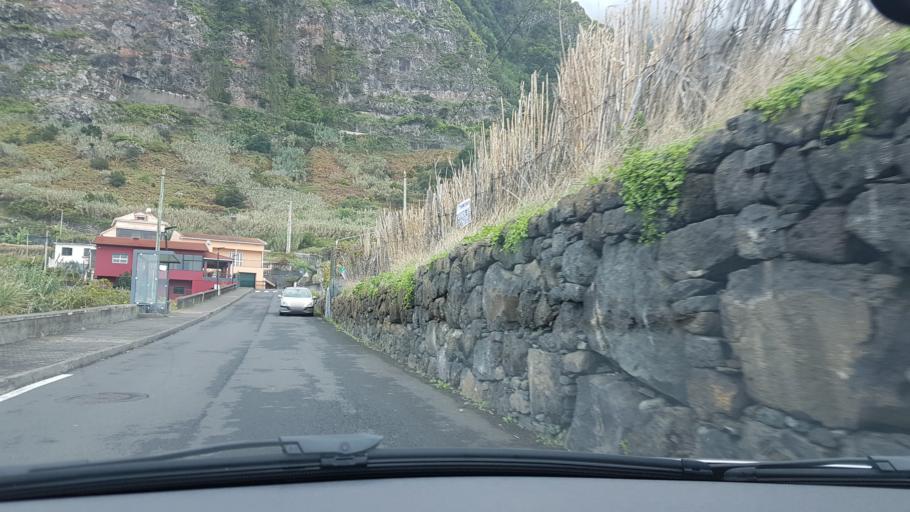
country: PT
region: Madeira
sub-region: Sao Vicente
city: Sao Vicente
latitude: 32.8276
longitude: -16.9853
